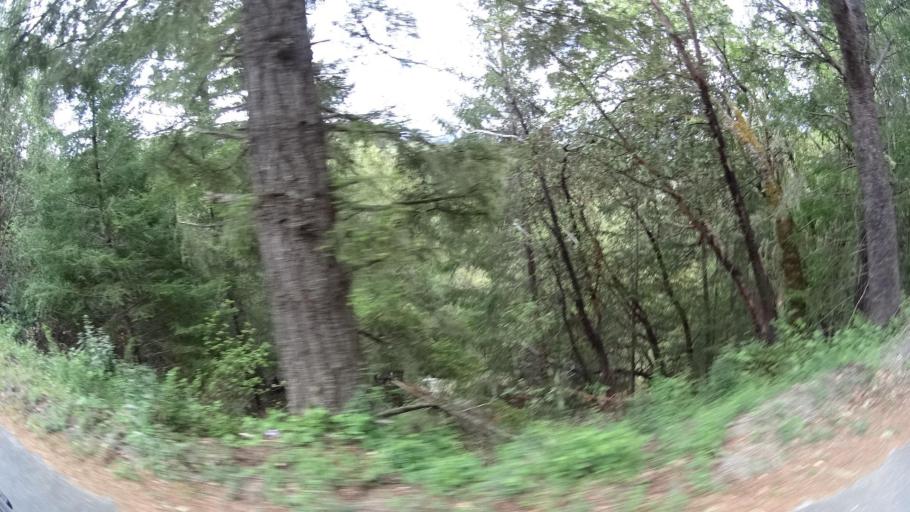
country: US
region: California
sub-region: Humboldt County
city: Redway
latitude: 40.1710
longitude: -123.5675
